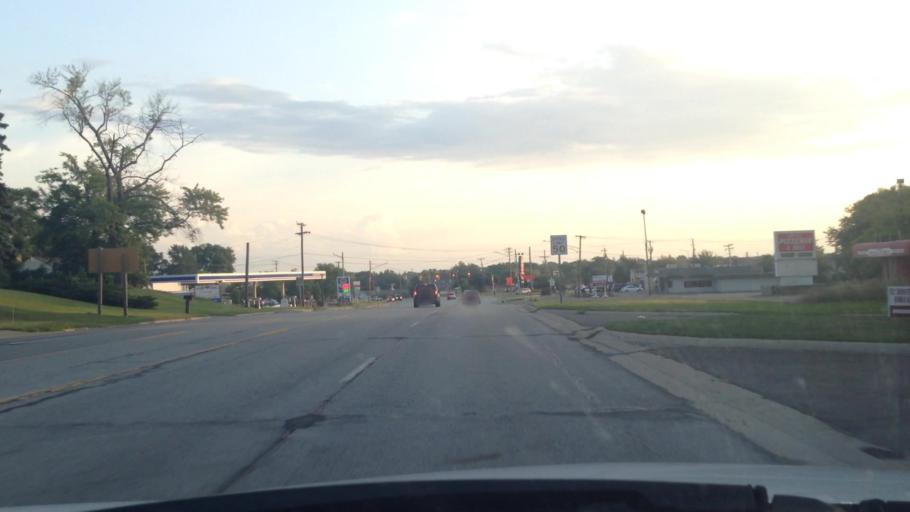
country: US
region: Michigan
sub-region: Oakland County
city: Auburn Hills
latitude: 42.6798
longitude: -83.2489
